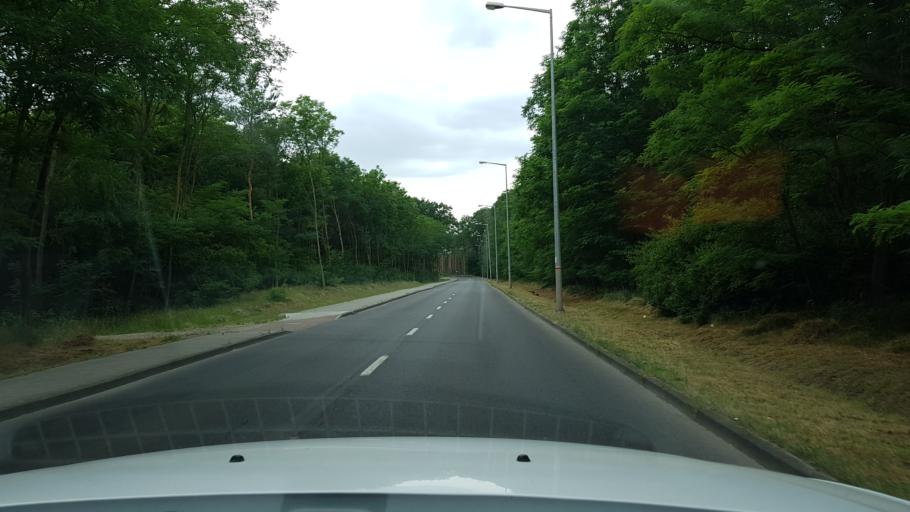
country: PL
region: Lubusz
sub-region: Powiat gorzowski
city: Kostrzyn nad Odra
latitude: 52.6189
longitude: 14.6105
